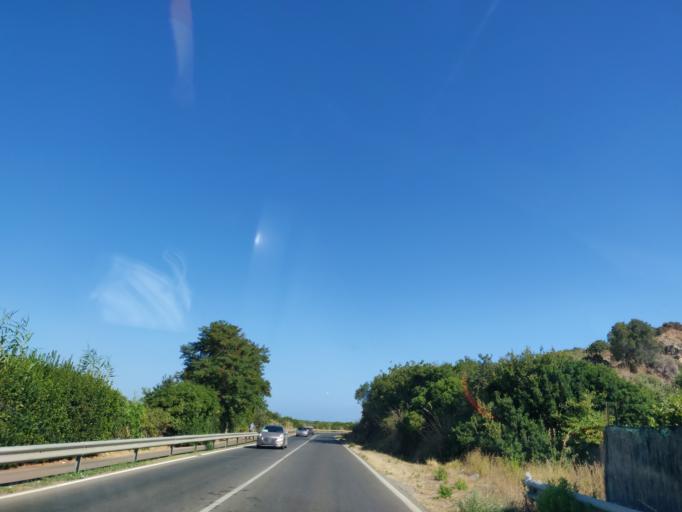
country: IT
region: Tuscany
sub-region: Provincia di Grosseto
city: Porto Ercole
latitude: 42.4246
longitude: 11.1998
